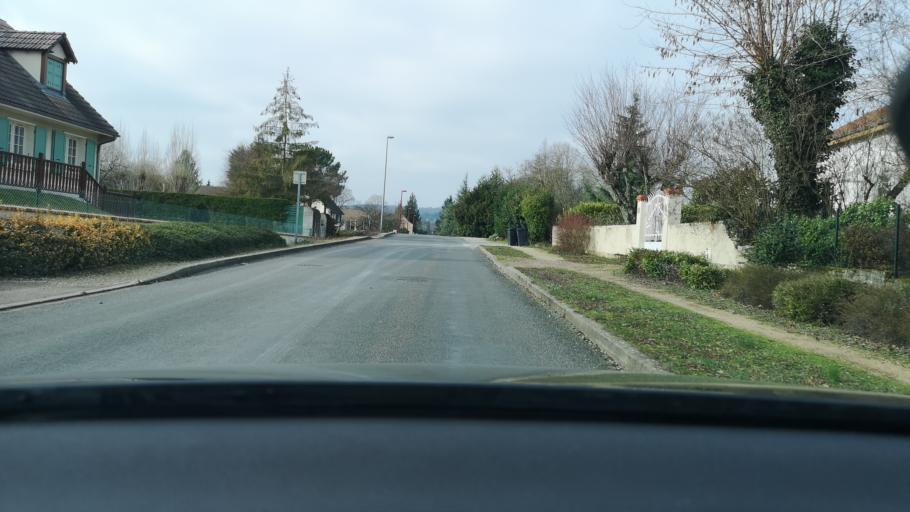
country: FR
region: Bourgogne
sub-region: Departement de Saone-et-Loire
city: Givry
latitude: 46.7777
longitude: 4.7485
